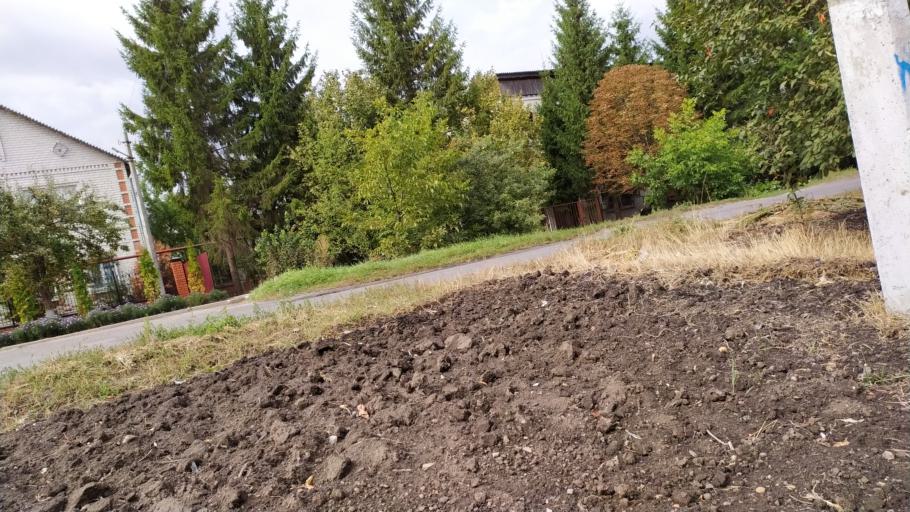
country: RU
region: Kursk
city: Kursk
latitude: 51.6410
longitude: 36.1391
